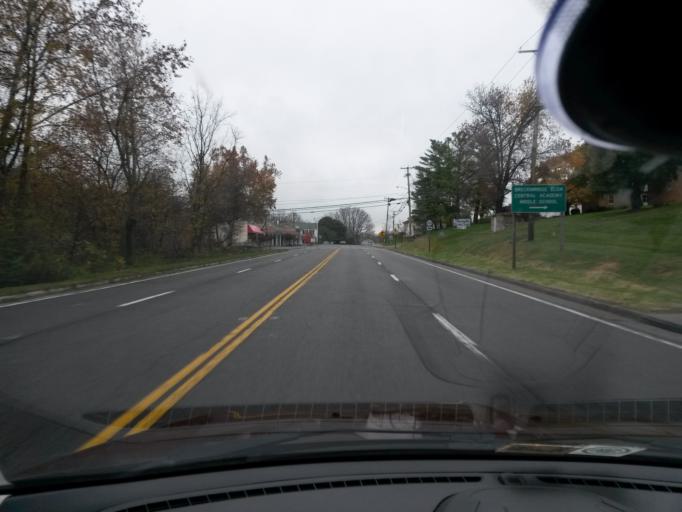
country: US
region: Virginia
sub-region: Botetourt County
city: Fincastle
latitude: 37.4980
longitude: -79.8794
